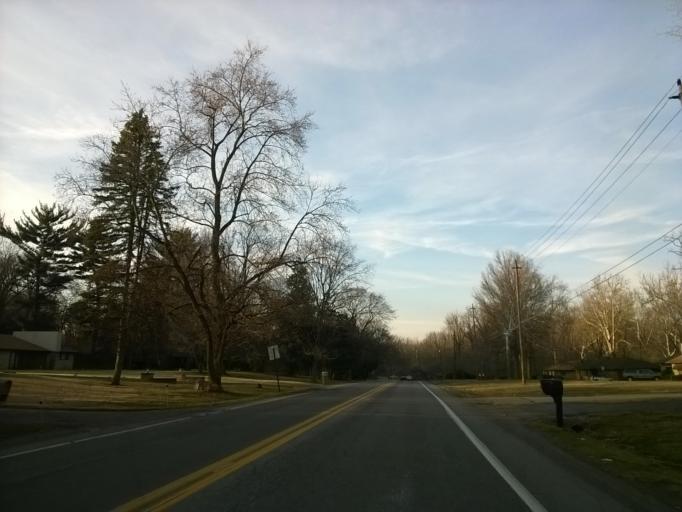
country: US
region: Indiana
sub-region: Marion County
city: Speedway
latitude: 39.8322
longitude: -86.2117
